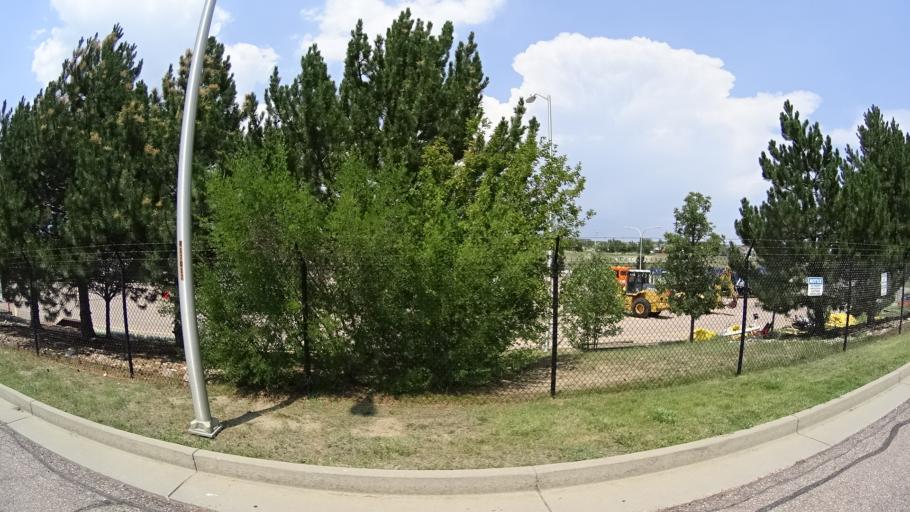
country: US
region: Colorado
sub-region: El Paso County
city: Black Forest
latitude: 38.9439
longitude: -104.7255
